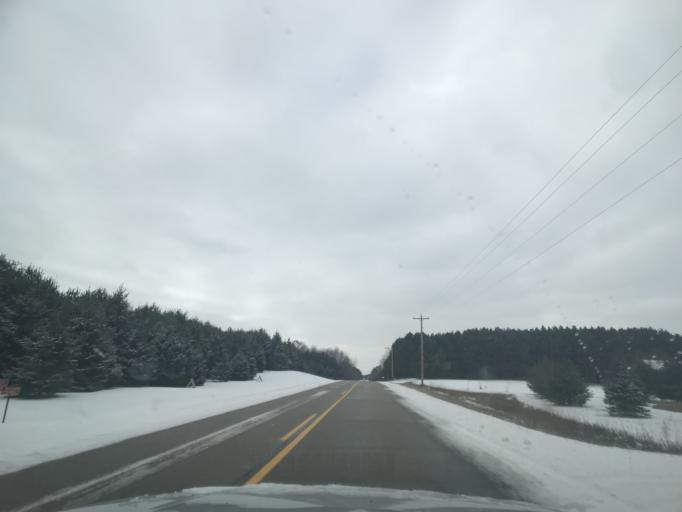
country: US
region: Wisconsin
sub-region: Brown County
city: Suamico
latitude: 44.7062
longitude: -88.0914
